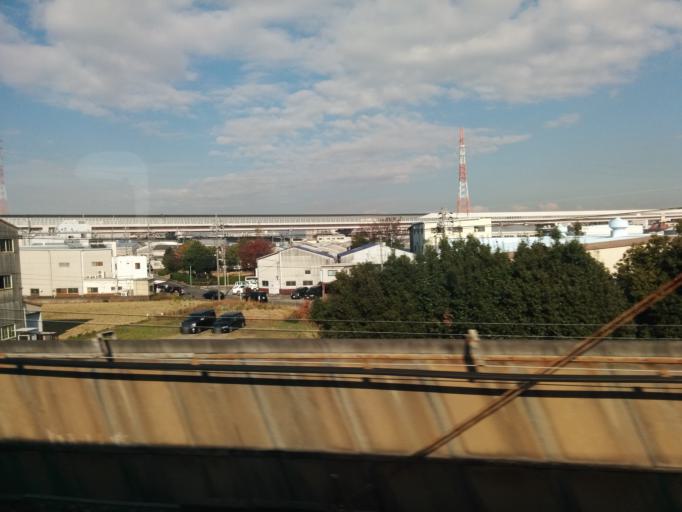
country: JP
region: Aichi
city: Obu
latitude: 35.0403
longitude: 136.9616
